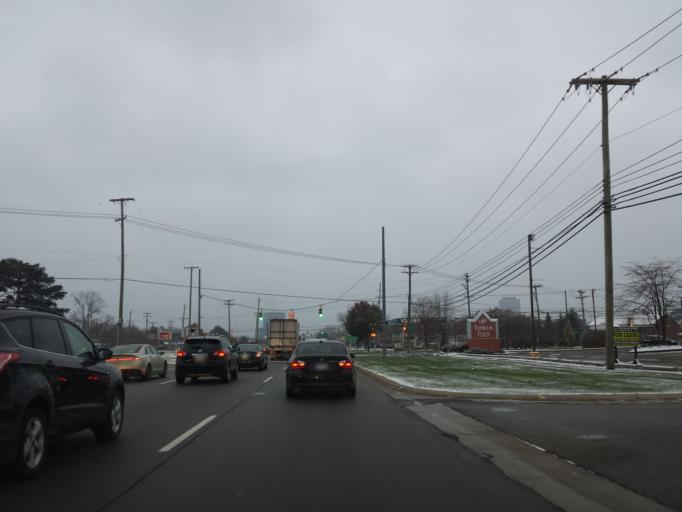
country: US
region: Michigan
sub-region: Oakland County
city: Franklin
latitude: 42.5017
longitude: -83.3105
